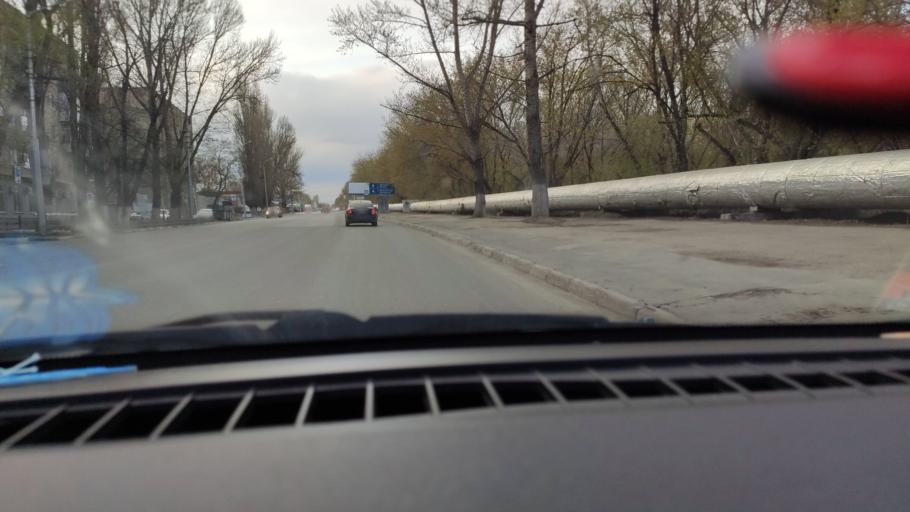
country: RU
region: Saratov
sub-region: Saratovskiy Rayon
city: Saratov
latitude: 51.5562
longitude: 46.0067
